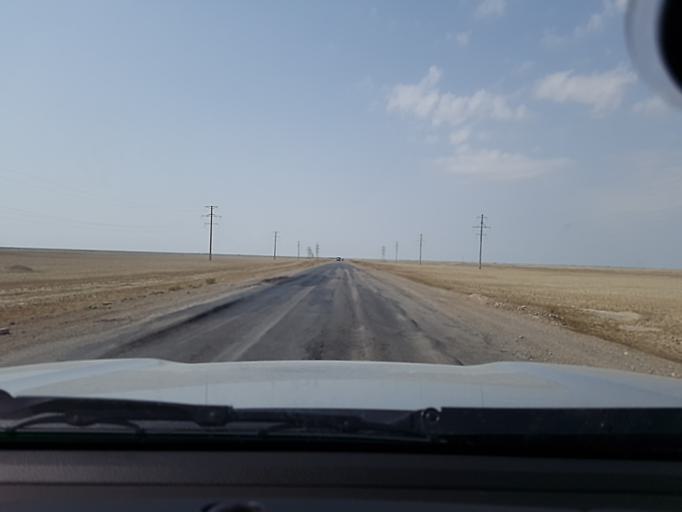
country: TM
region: Balkan
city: Gumdag
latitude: 39.0600
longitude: 54.5844
